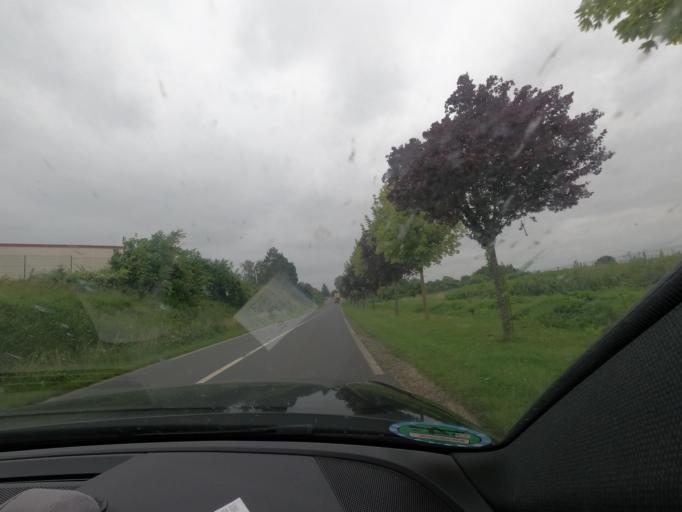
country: FR
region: Picardie
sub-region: Departement de l'Oise
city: Ressons-sur-Matz
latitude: 49.5396
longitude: 2.7354
